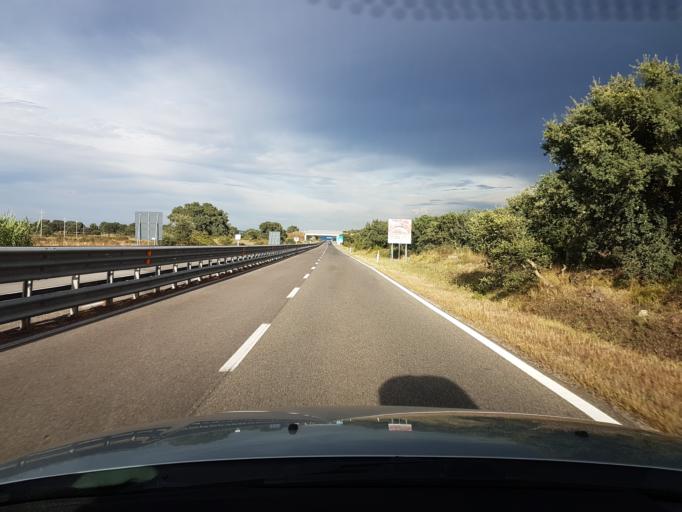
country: IT
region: Sardinia
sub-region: Provincia di Oristano
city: Abbasanta
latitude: 40.1137
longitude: 8.8036
